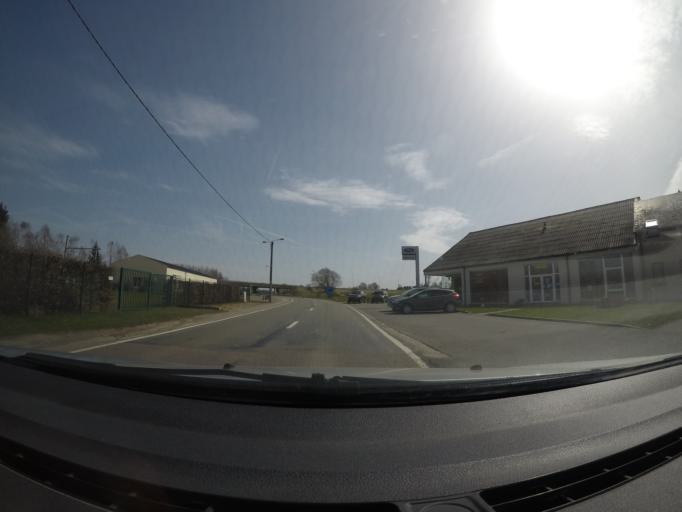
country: BE
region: Wallonia
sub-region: Province du Luxembourg
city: Habay-la-Vieille
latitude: 49.7192
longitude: 5.5896
